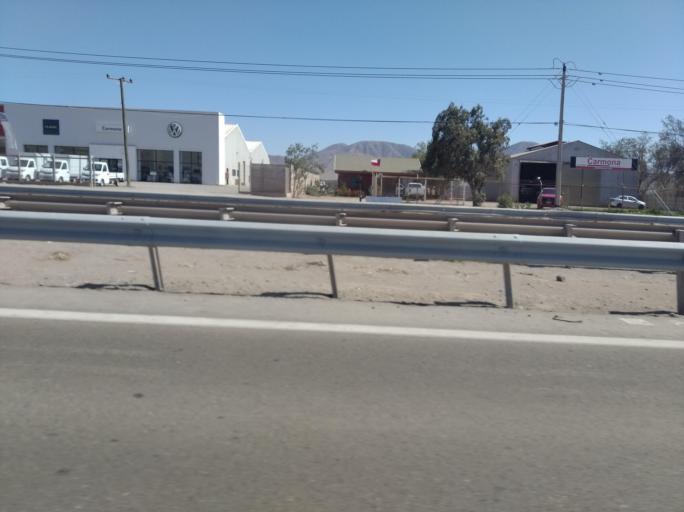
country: CL
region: Atacama
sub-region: Provincia de Copiapo
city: Copiapo
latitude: -27.3306
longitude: -70.3852
